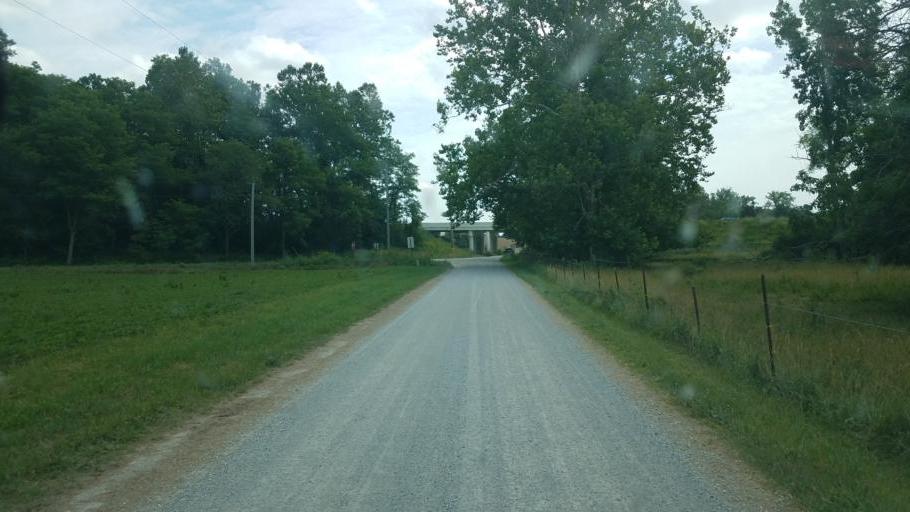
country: US
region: Ohio
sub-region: Knox County
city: Fredericktown
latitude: 40.5604
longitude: -82.6436
